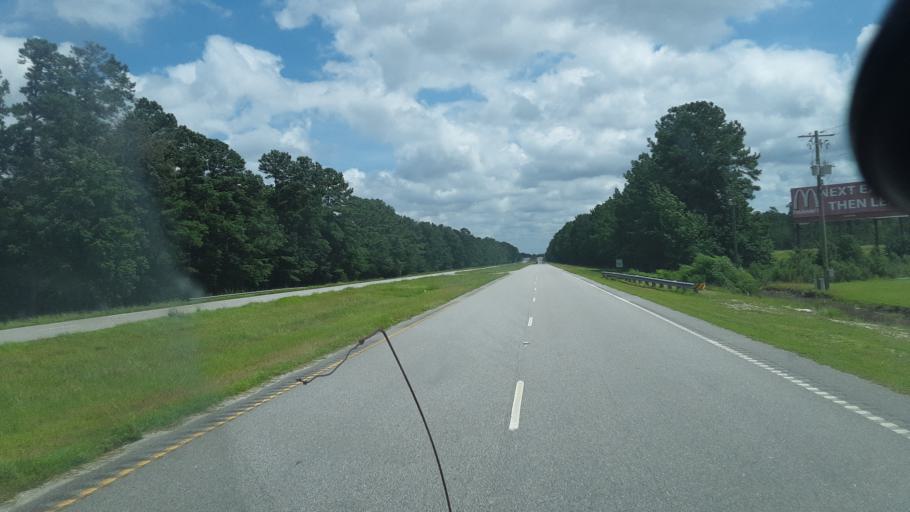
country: US
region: South Carolina
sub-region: Horry County
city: Loris
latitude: 34.0876
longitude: -78.8903
